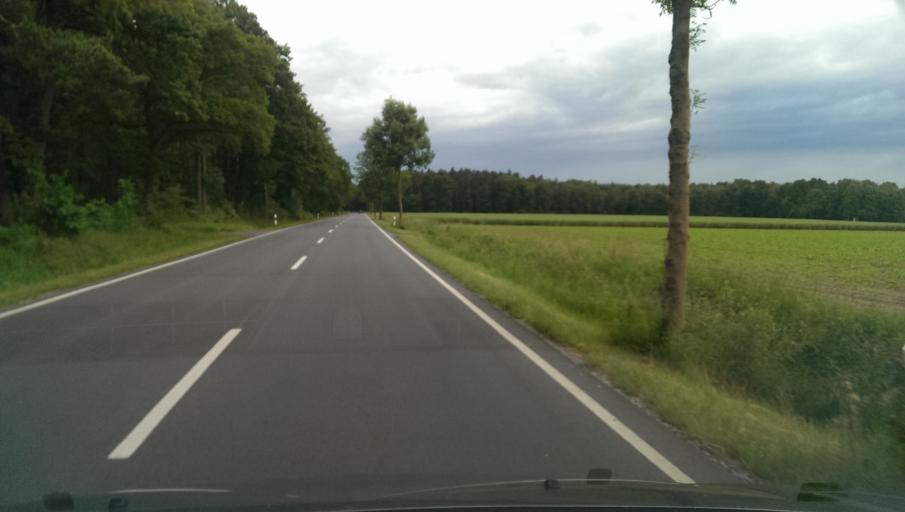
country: DE
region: Lower Saxony
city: Parsau
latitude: 52.5201
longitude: 10.8883
